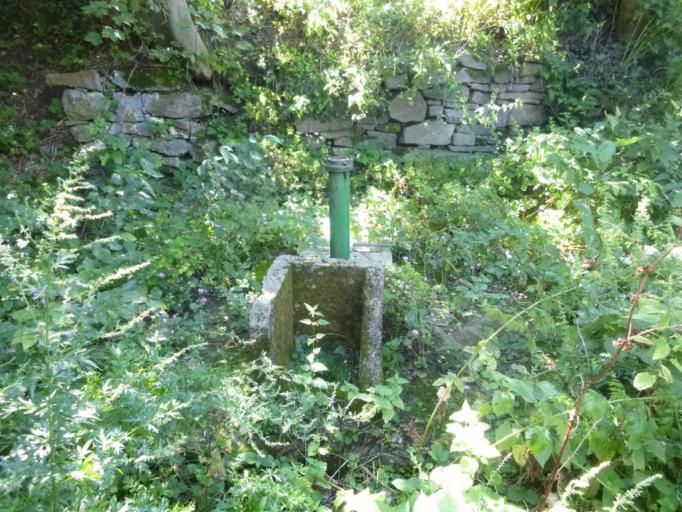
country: HU
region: Baranya
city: Pellerd
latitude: 46.0950
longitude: 18.1435
